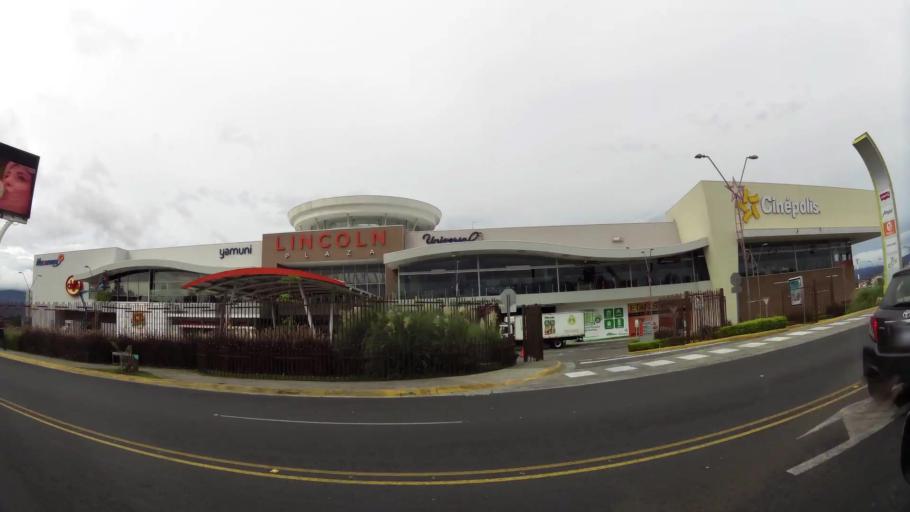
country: CR
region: San Jose
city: San Vicente de Moravia
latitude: 9.9624
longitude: -84.0550
